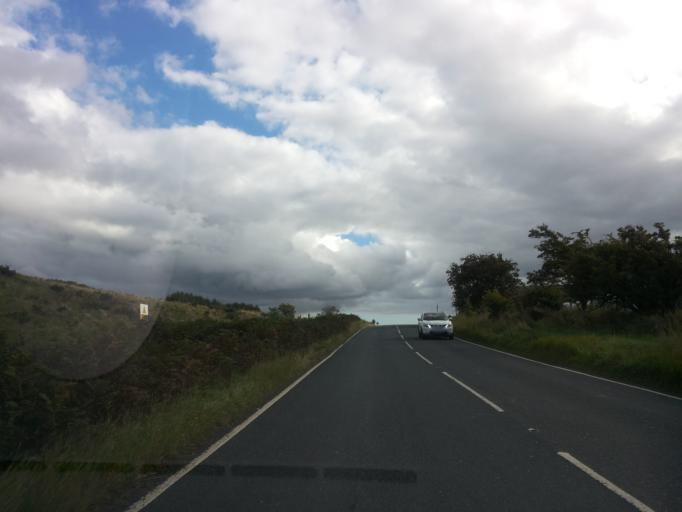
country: GB
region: England
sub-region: North Yorkshire
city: Leyburn
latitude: 54.3501
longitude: -1.7982
